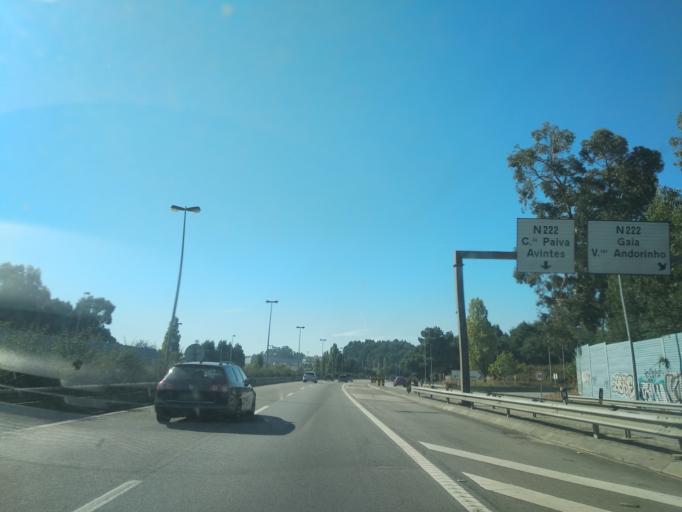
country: PT
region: Porto
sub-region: Vila Nova de Gaia
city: Avintes
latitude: 41.1041
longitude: -8.5668
